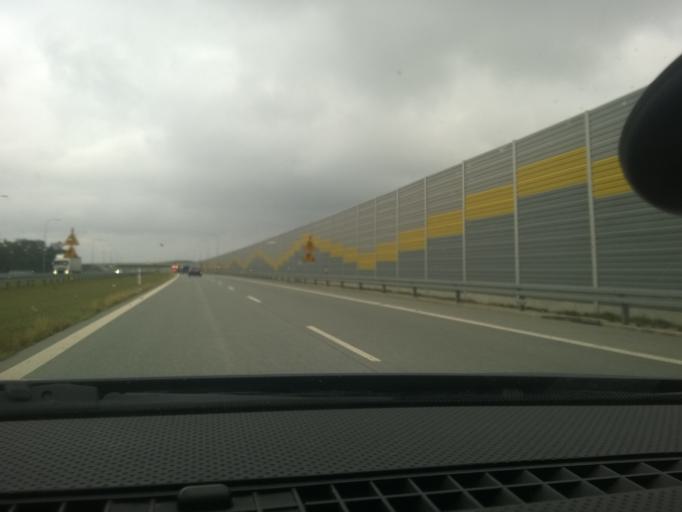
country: PL
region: Lodz Voivodeship
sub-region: Powiat laski
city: Lask
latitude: 51.5537
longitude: 19.0791
